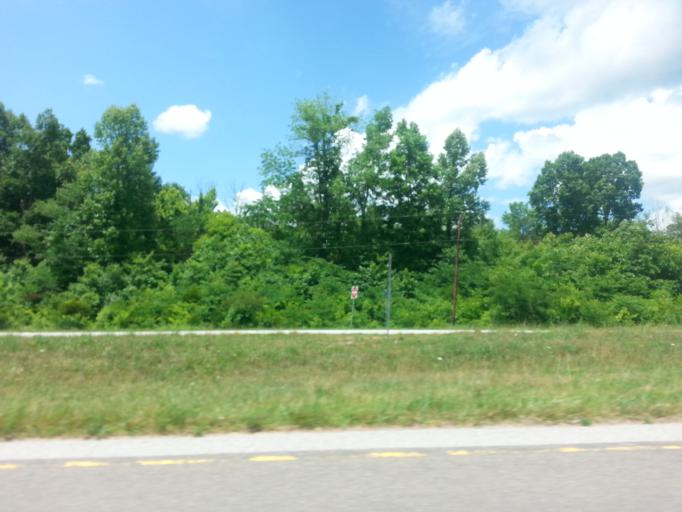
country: US
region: Tennessee
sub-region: Claiborne County
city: Harrogate
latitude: 36.6164
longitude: -83.5608
